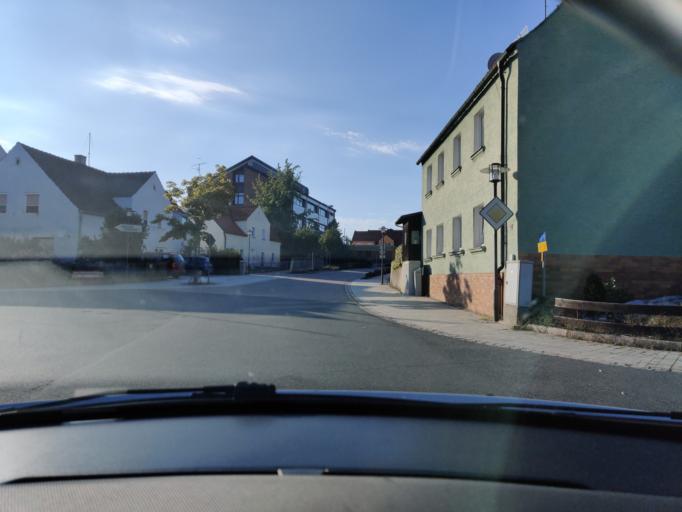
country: DE
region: Bavaria
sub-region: Upper Palatinate
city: Schwarzenfeld
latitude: 49.3905
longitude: 12.1382
